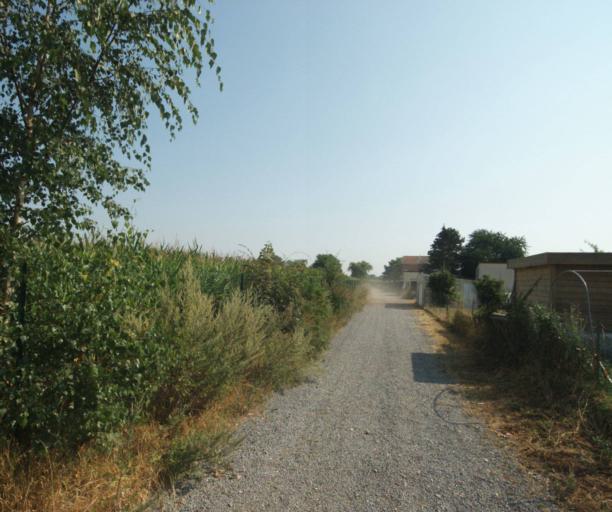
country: FR
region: Nord-Pas-de-Calais
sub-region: Departement du Nord
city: Quesnoy-sur-Deule
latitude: 50.7032
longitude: 3.0043
